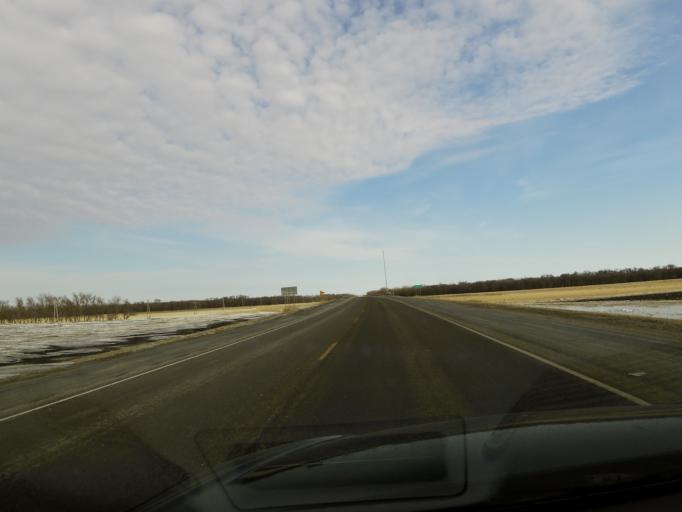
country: US
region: North Dakota
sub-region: Walsh County
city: Grafton
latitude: 48.5715
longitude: -97.1642
